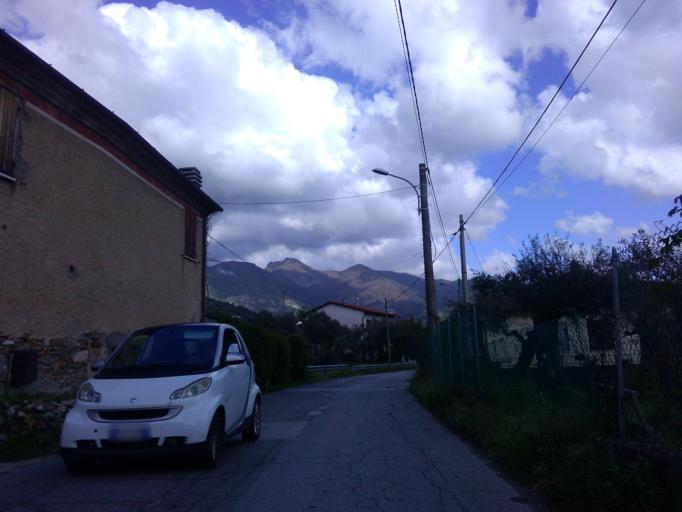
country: IT
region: Tuscany
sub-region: Provincia di Lucca
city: Strettoia
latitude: 43.9876
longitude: 10.2015
